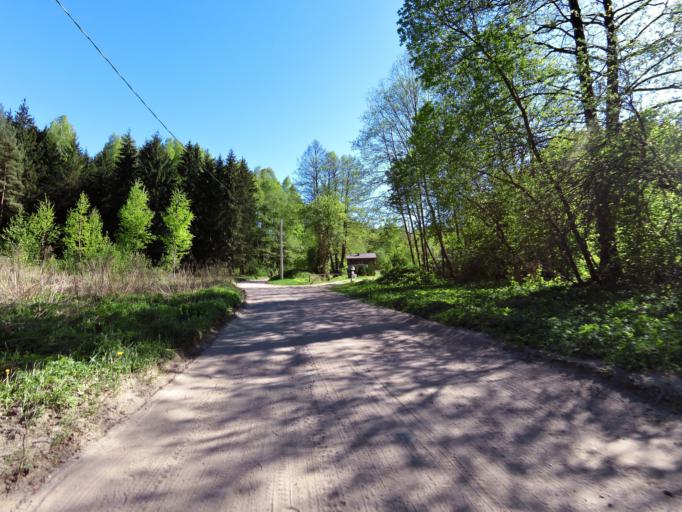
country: LT
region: Vilnius County
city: Pilaite
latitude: 54.6885
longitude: 25.1556
